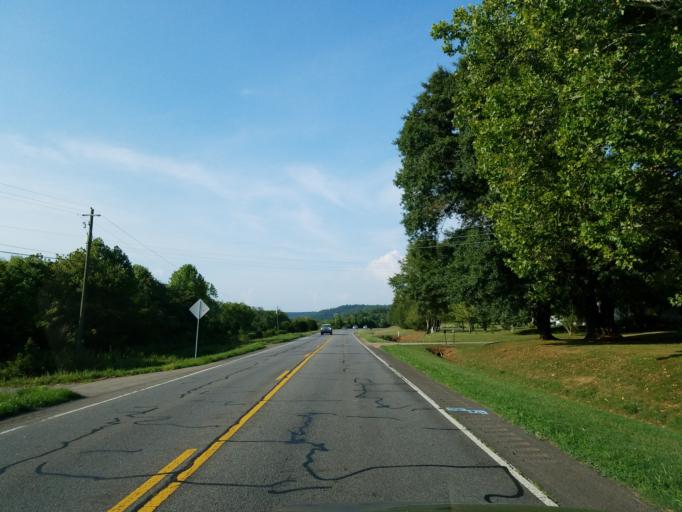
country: US
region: Georgia
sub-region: Bartow County
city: Rydal
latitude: 34.4014
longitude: -84.7082
